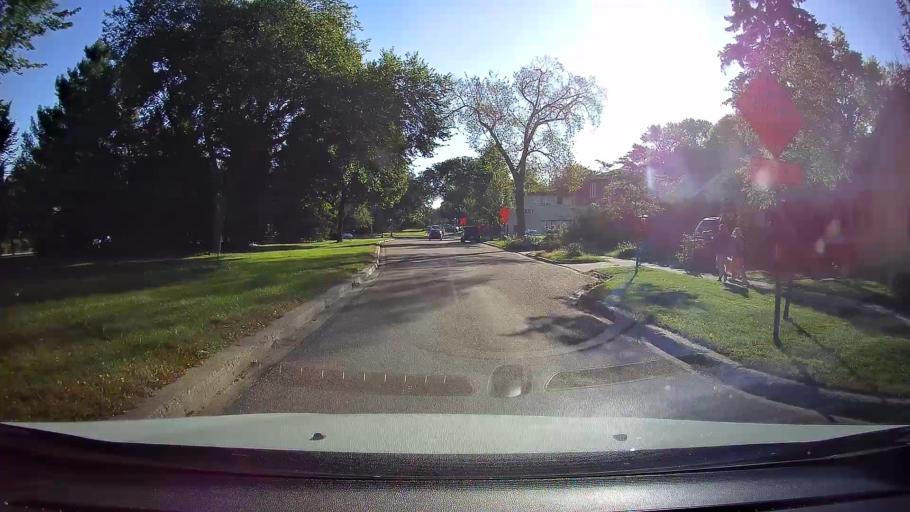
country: US
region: Minnesota
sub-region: Hennepin County
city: Richfield
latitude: 44.9161
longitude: -93.2335
